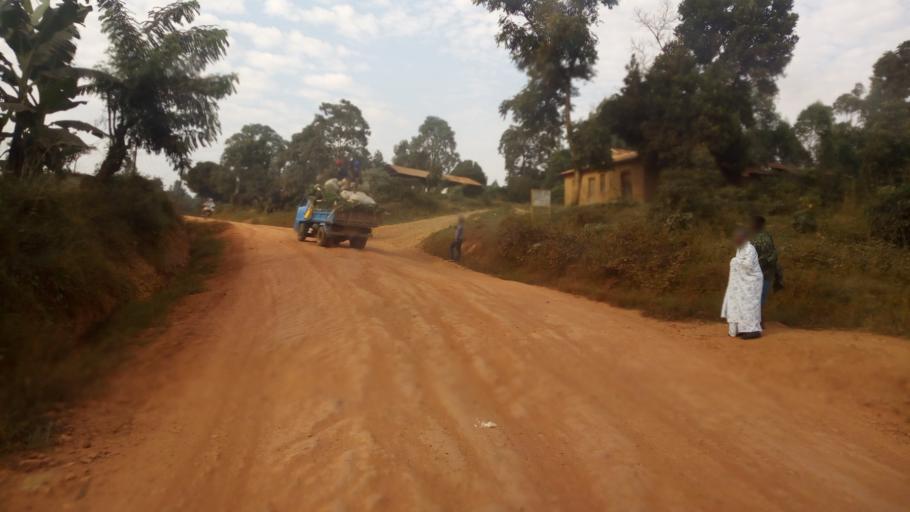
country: UG
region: Western Region
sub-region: Kanungu District
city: Ntungamo
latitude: -0.8462
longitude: 29.6414
